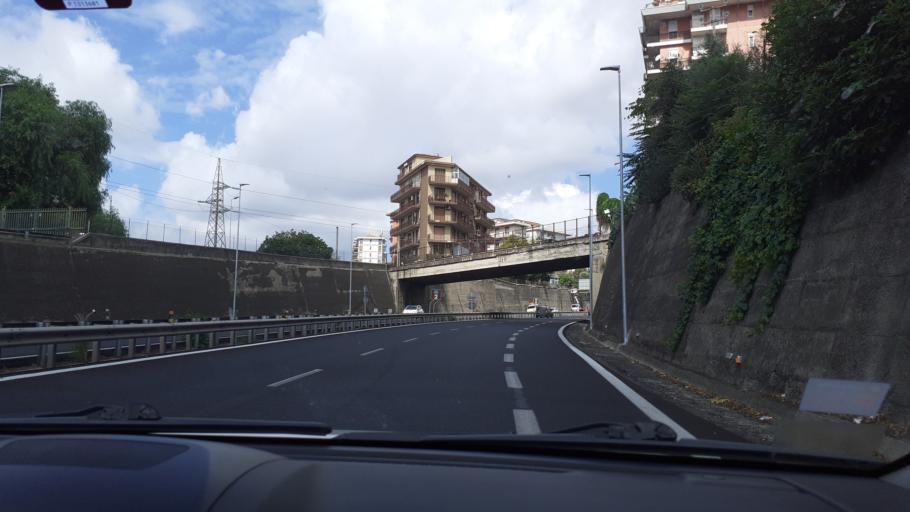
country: IT
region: Sicily
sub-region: Catania
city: Canalicchio
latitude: 37.5373
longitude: 15.0942
